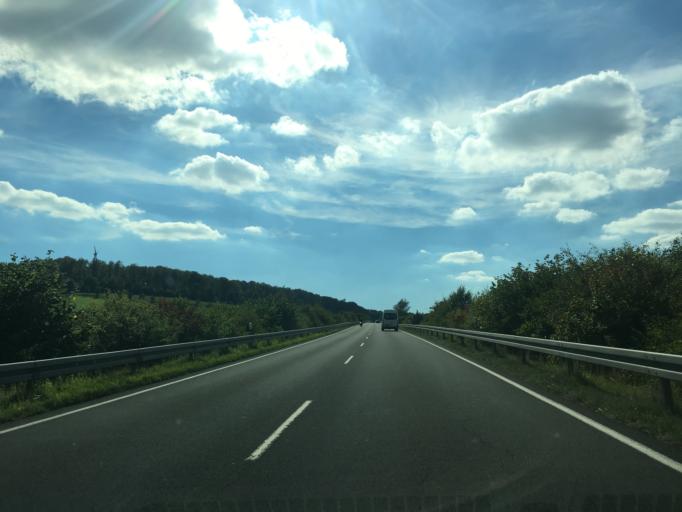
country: DE
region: North Rhine-Westphalia
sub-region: Regierungsbezirk Detmold
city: Lemgo
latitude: 52.0050
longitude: 8.9411
